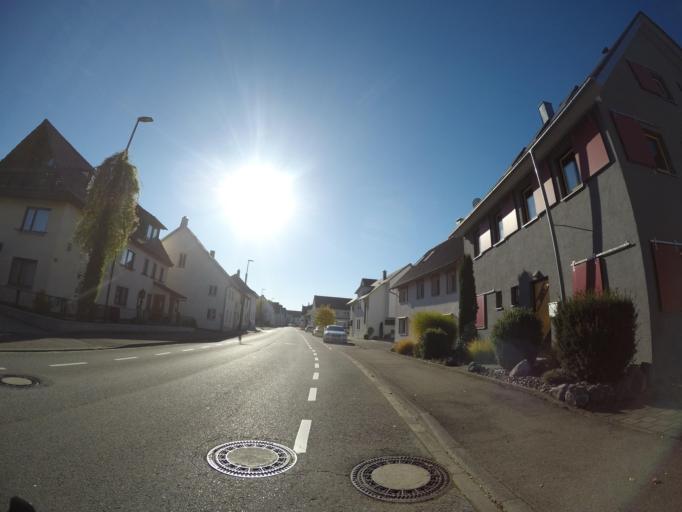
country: DE
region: Baden-Wuerttemberg
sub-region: Tuebingen Region
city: Saulgau
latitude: 48.0207
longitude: 9.4965
